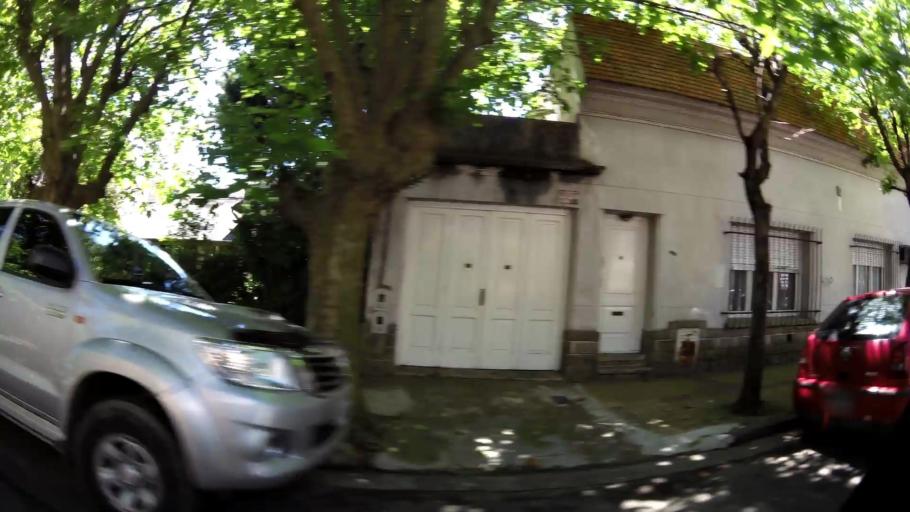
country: AR
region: Buenos Aires
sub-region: Partido de Quilmes
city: Quilmes
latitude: -34.7175
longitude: -58.2555
